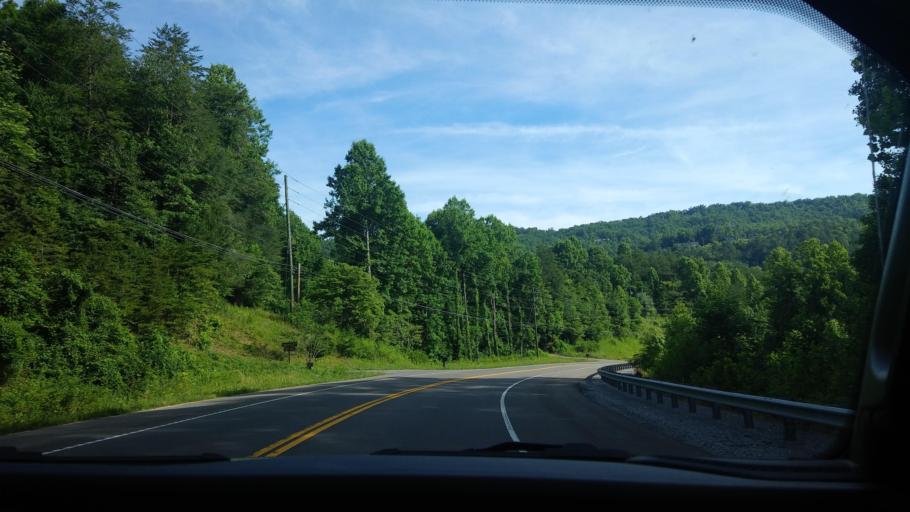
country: US
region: Tennessee
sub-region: Sevier County
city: Gatlinburg
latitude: 35.7556
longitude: -83.3849
